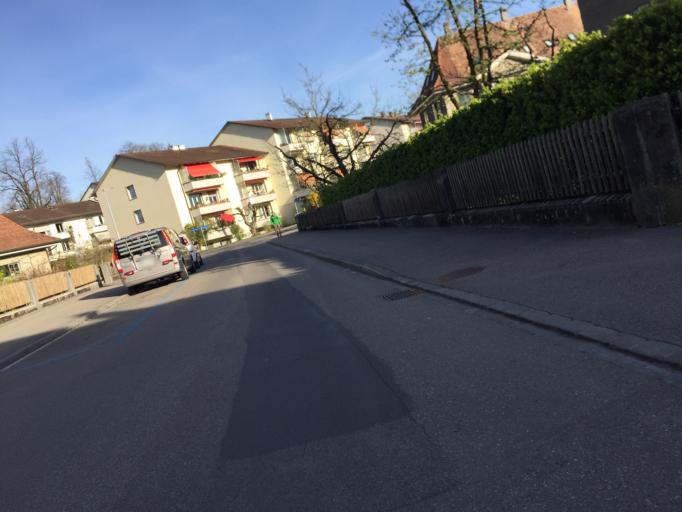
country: CH
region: Bern
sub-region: Bern-Mittelland District
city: Koniz
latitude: 46.9386
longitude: 7.4218
